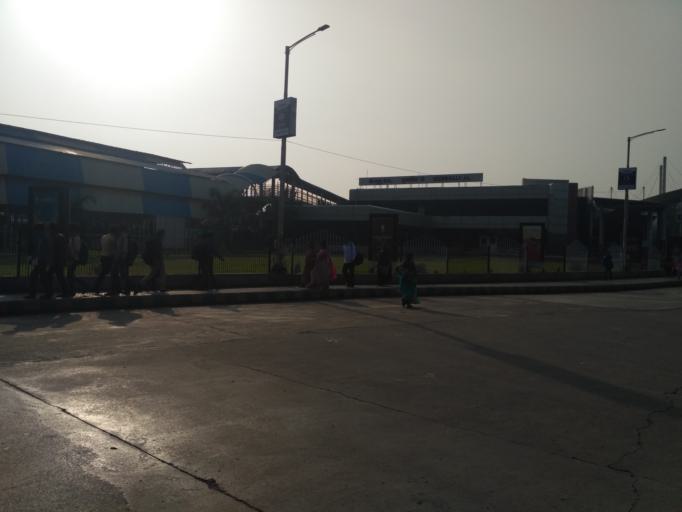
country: IN
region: Karnataka
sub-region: Dharwad
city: Hubli
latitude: 15.3508
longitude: 75.1479
